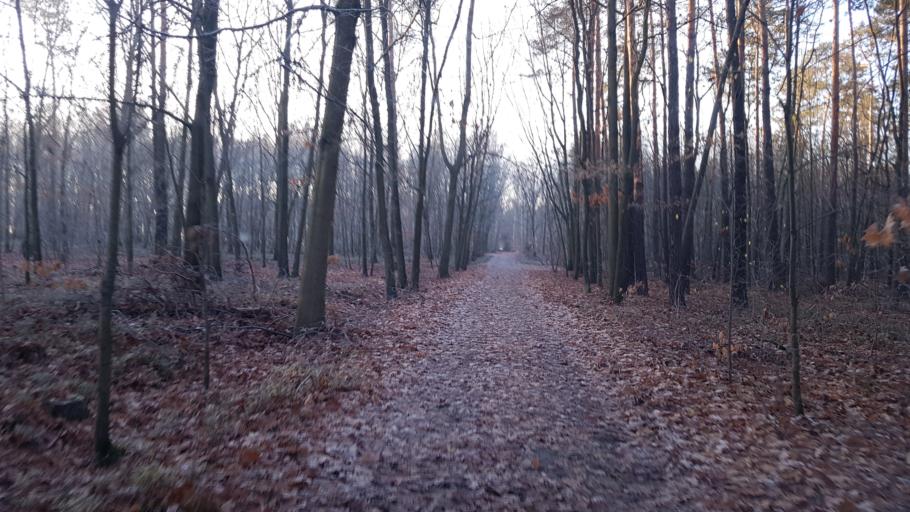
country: DE
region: Brandenburg
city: Sallgast
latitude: 51.5984
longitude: 13.8368
